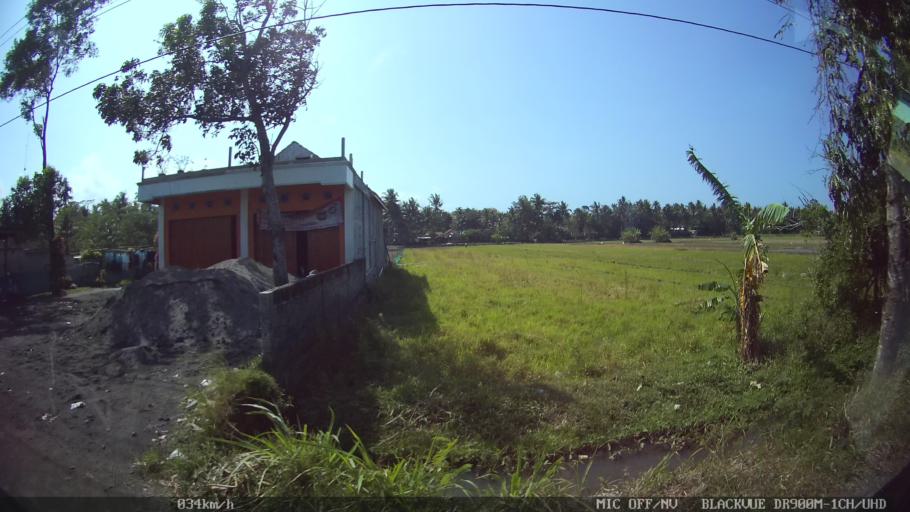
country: ID
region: Daerah Istimewa Yogyakarta
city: Srandakan
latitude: -7.9575
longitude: 110.2148
